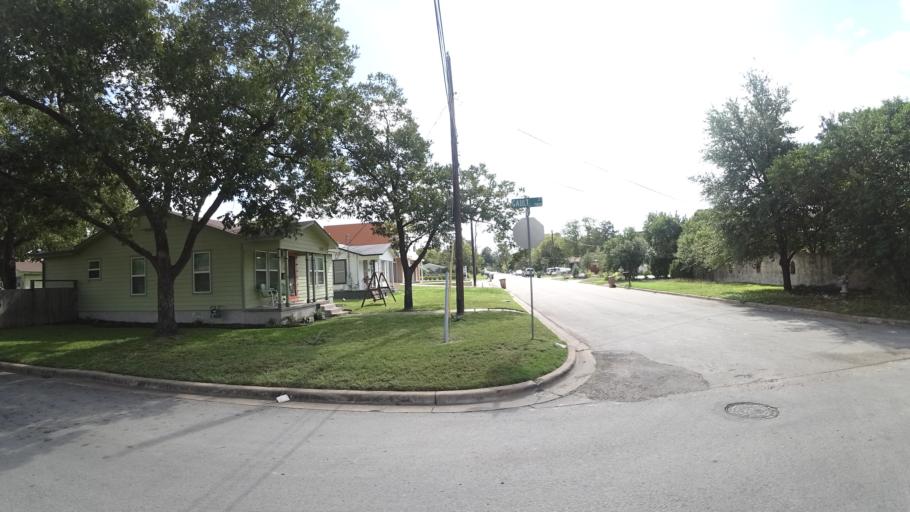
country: US
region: Texas
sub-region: Travis County
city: Austin
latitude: 30.3492
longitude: -97.7193
